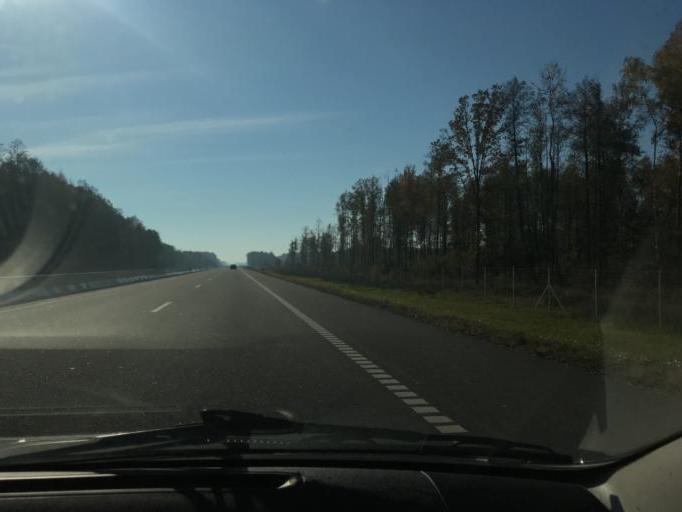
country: BY
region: Minsk
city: Slutsk
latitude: 53.2544
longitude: 27.5501
